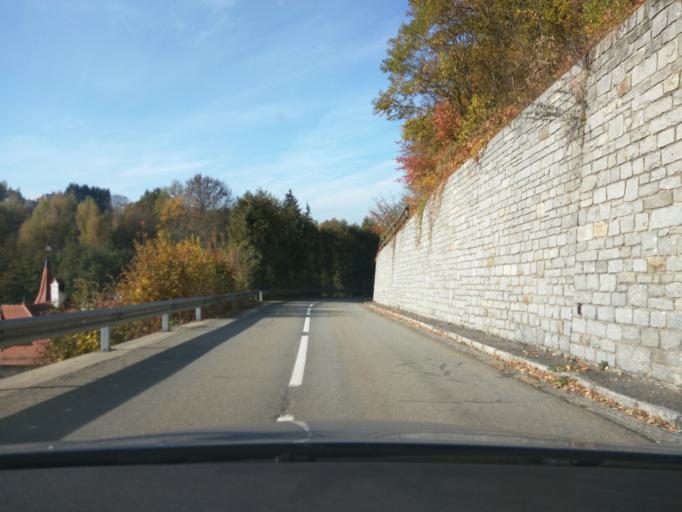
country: DE
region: Bavaria
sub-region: Lower Bavaria
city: Salzweg
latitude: 48.5670
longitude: 13.4944
